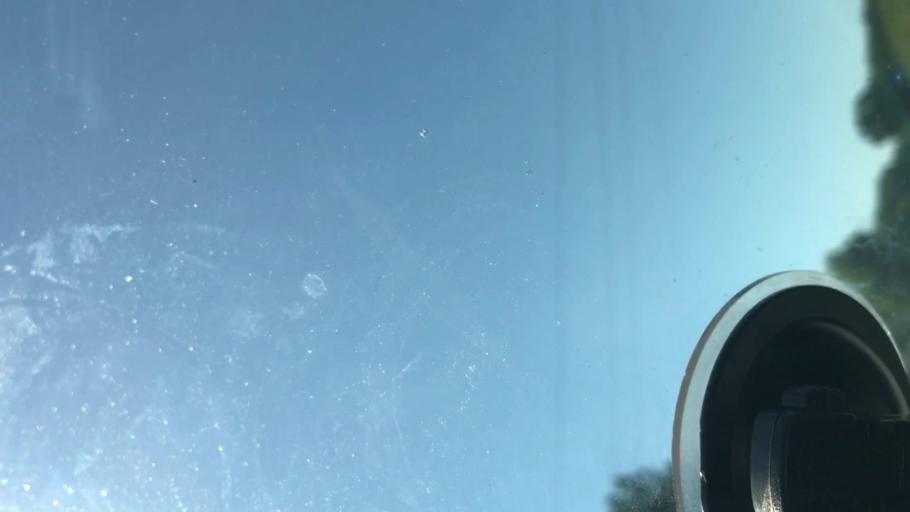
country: US
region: Virginia
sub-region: Spotsylvania County
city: Spotsylvania Courthouse
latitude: 38.1465
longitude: -77.5242
